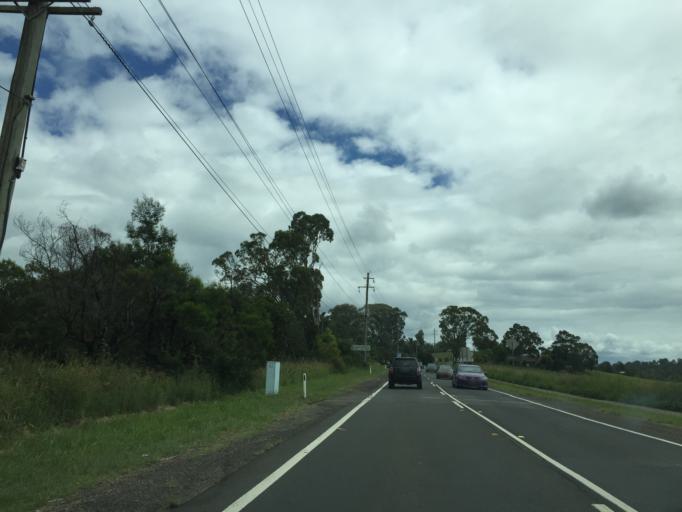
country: AU
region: New South Wales
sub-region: Hawkesbury
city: Richmond
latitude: -33.5686
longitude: 150.7047
